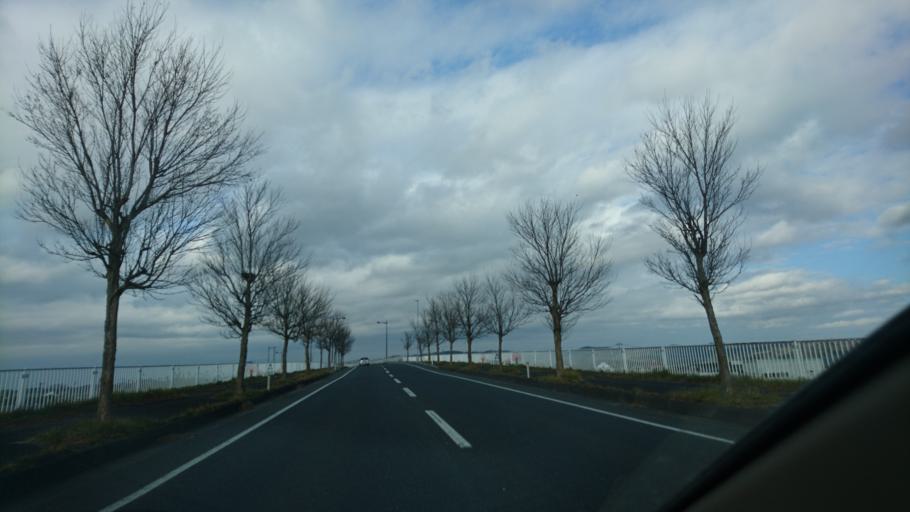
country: JP
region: Miyagi
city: Wakuya
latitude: 38.5449
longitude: 141.1082
